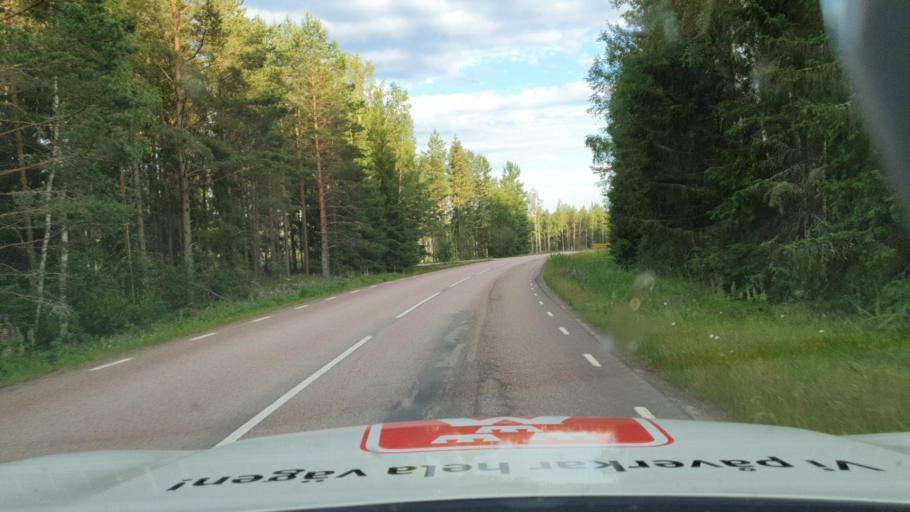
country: SE
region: Vaermland
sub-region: Karlstads Kommun
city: Molkom
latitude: 59.5013
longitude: 13.7971
